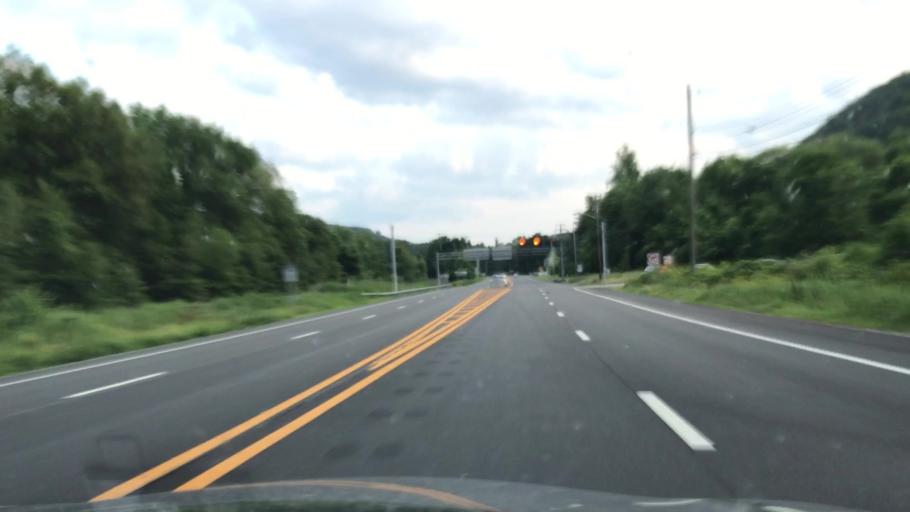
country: US
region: New York
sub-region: Rockland County
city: Sloatsburg
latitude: 41.2282
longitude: -74.1849
